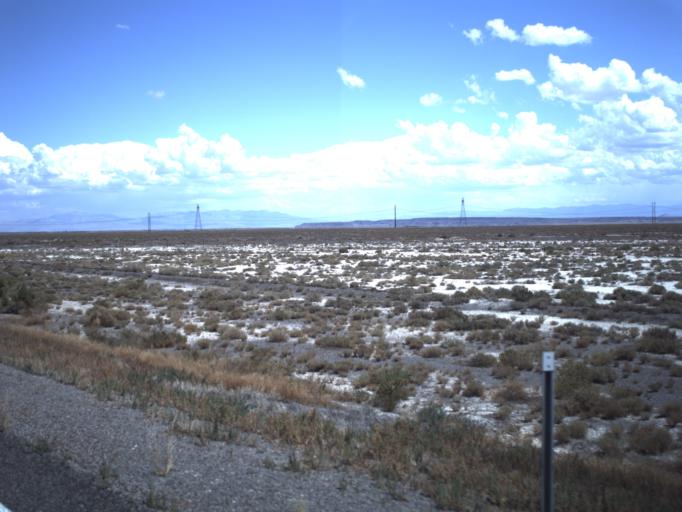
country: US
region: Utah
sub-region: Millard County
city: Delta
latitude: 39.2372
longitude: -112.9200
